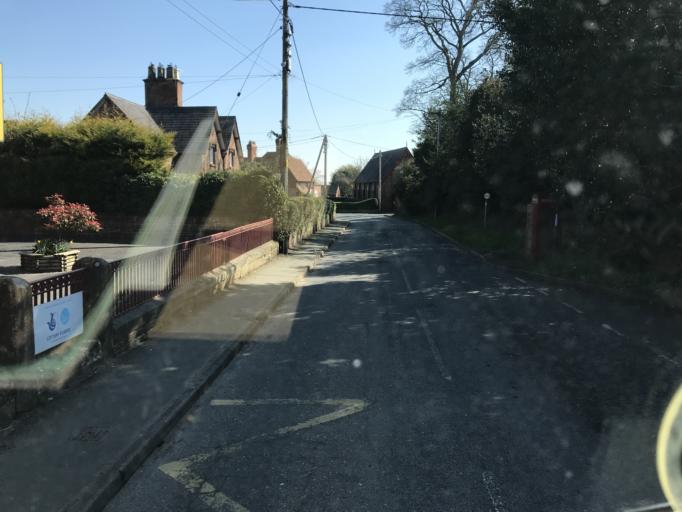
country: GB
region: England
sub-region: Cheshire West and Chester
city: Waverton
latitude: 53.1525
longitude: -2.8342
